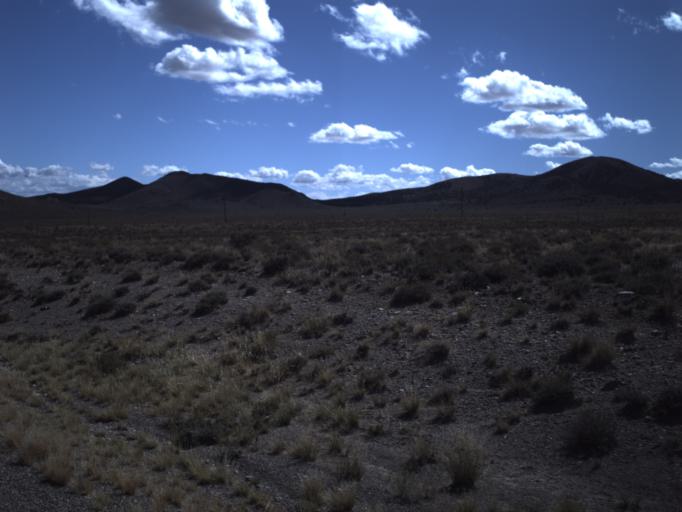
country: US
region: Utah
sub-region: Beaver County
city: Milford
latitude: 38.4286
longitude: -113.1231
